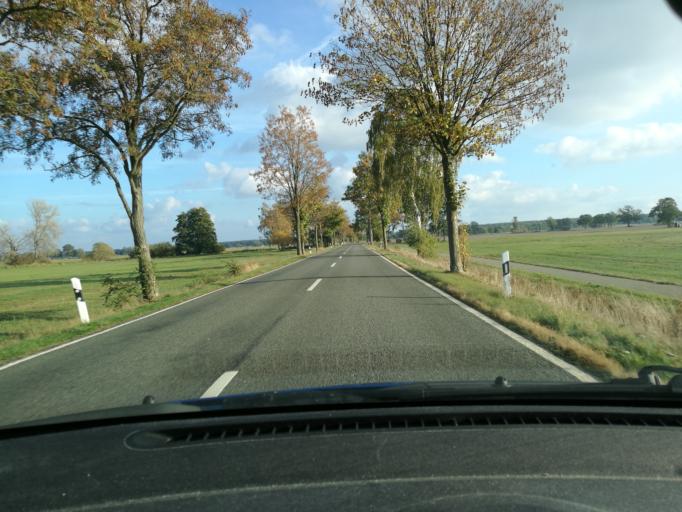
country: DE
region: Lower Saxony
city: Prezelle
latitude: 52.9029
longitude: 11.4217
